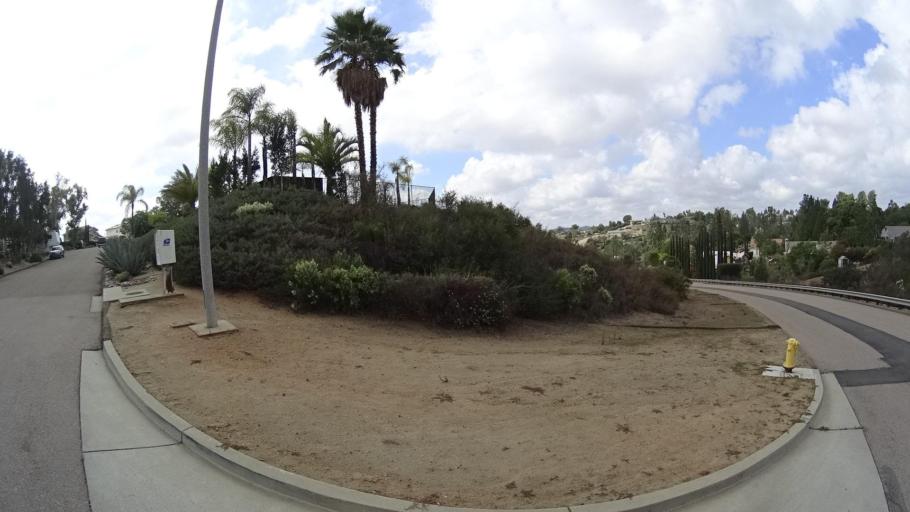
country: US
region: California
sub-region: San Diego County
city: Granite Hills
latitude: 32.7737
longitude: -116.9081
